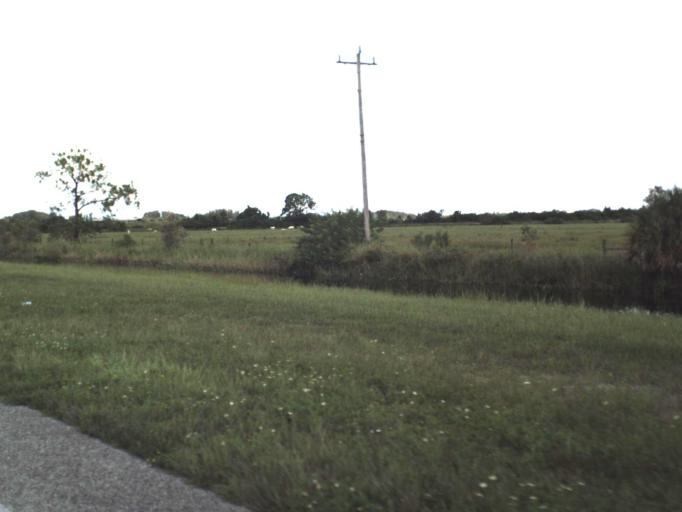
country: US
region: Florida
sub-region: Lee County
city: Suncoast Estates
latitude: 26.7815
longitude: -81.9385
